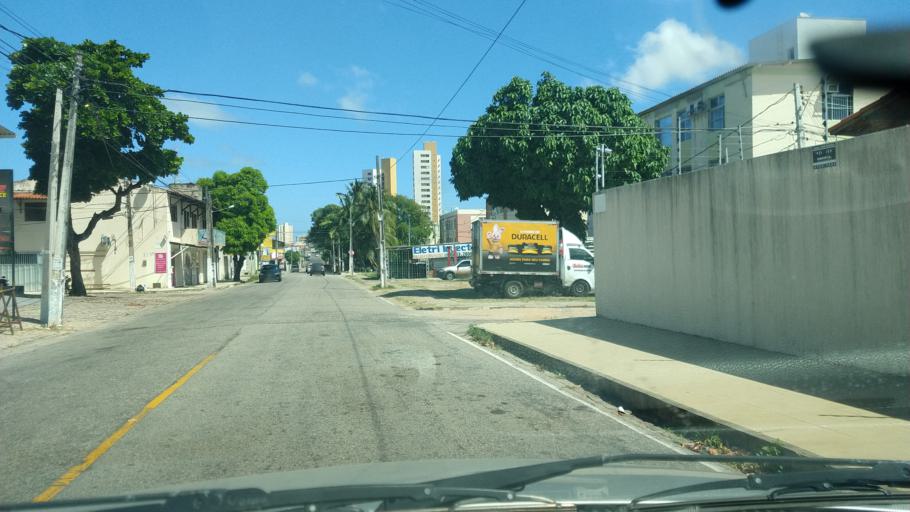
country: BR
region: Rio Grande do Norte
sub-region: Natal
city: Natal
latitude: -5.8575
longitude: -35.2119
